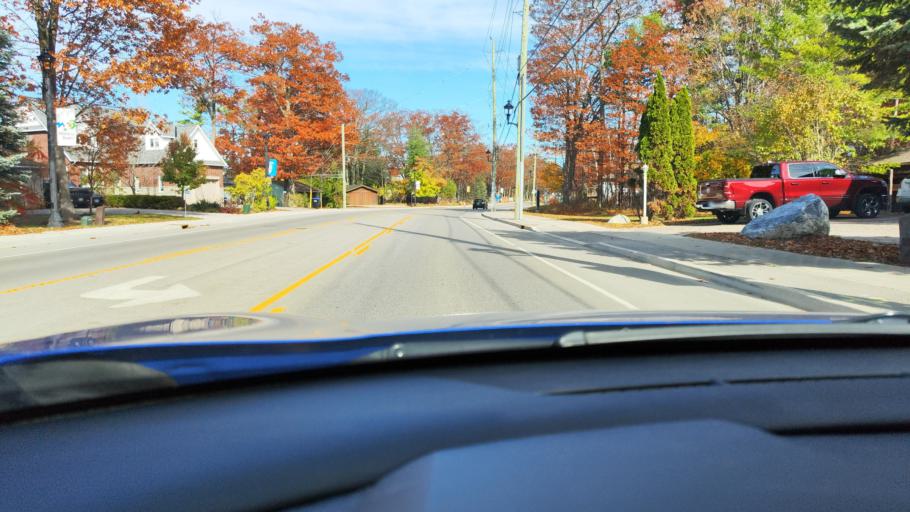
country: CA
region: Ontario
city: Wasaga Beach
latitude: 44.4957
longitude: -80.0424
